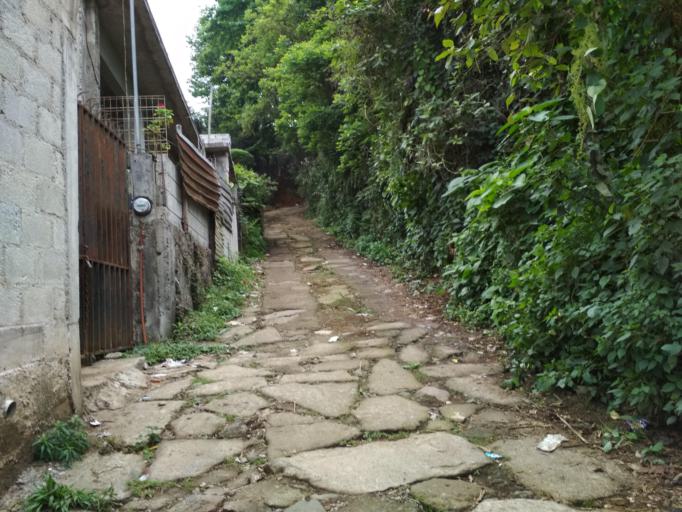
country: MX
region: Veracruz
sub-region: La Perla
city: La Perla
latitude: 18.9259
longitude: -97.1320
